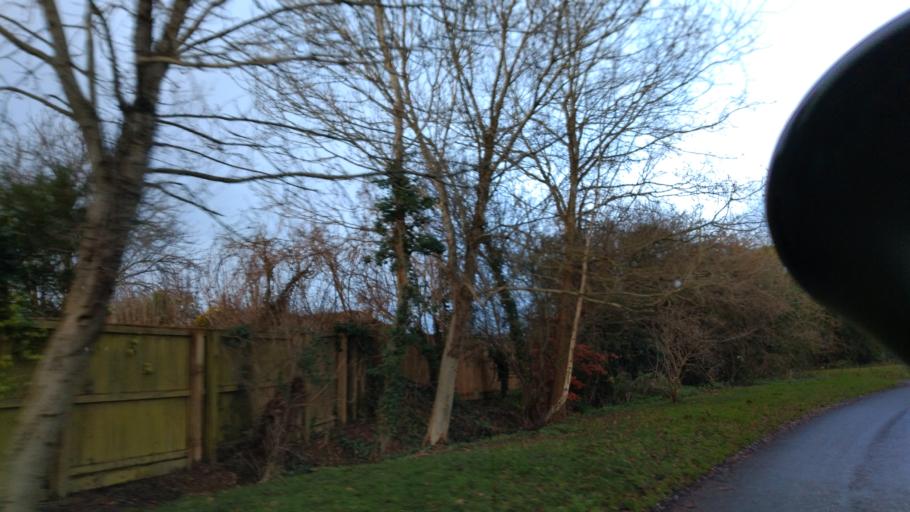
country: GB
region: England
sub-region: Wiltshire
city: Atworth
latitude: 51.3931
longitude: -2.1664
